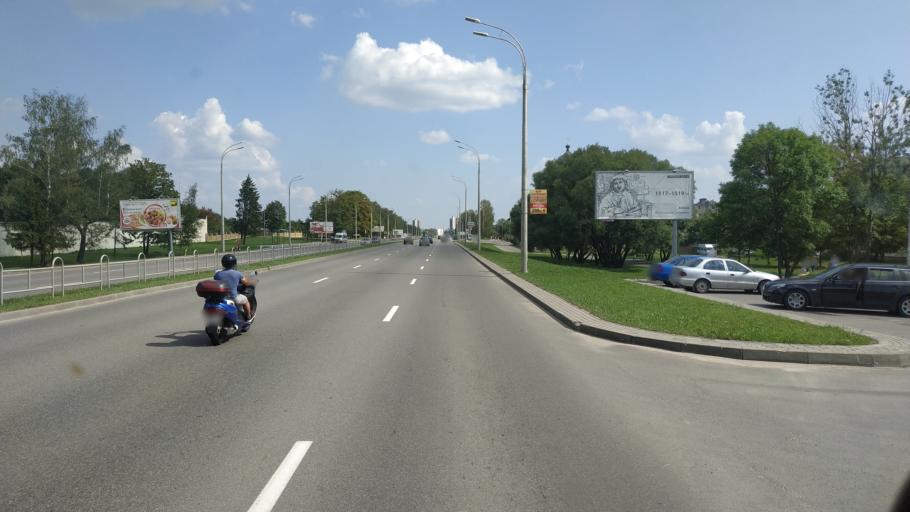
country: BY
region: Mogilev
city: Buynichy
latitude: 53.9319
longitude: 30.2601
